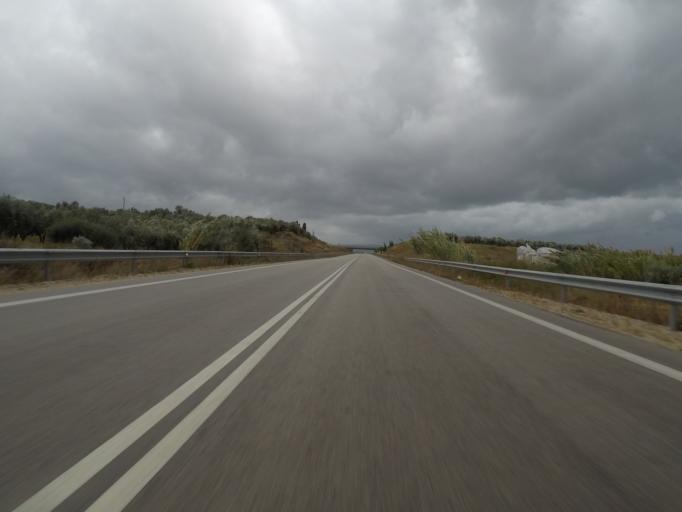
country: GR
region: Peloponnese
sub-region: Nomos Messinias
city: Gargalianoi
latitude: 37.0080
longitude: 21.6592
